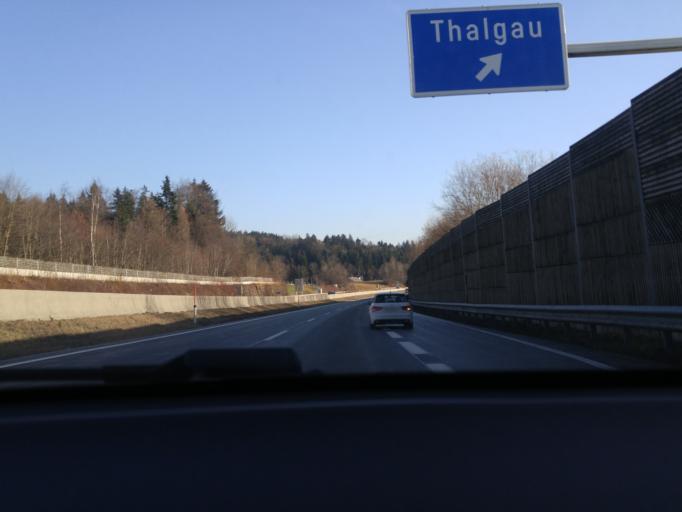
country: AT
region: Salzburg
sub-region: Politischer Bezirk Salzburg-Umgebung
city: Hof bei Salzburg
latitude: 47.8549
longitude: 13.2189
